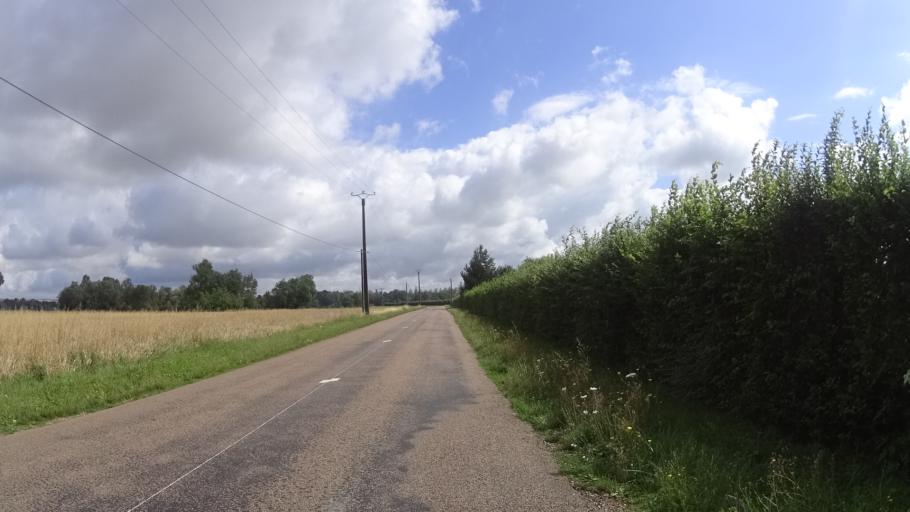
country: FR
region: Bourgogne
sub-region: Departement de l'Yonne
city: Saint-Florentin
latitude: 47.9843
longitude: 3.7692
